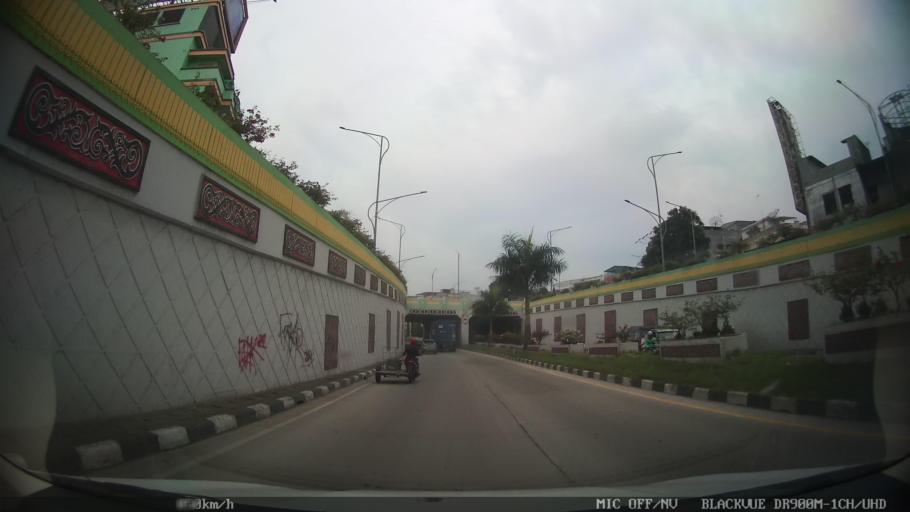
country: ID
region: North Sumatra
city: Deli Tua
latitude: 3.5389
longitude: 98.6838
